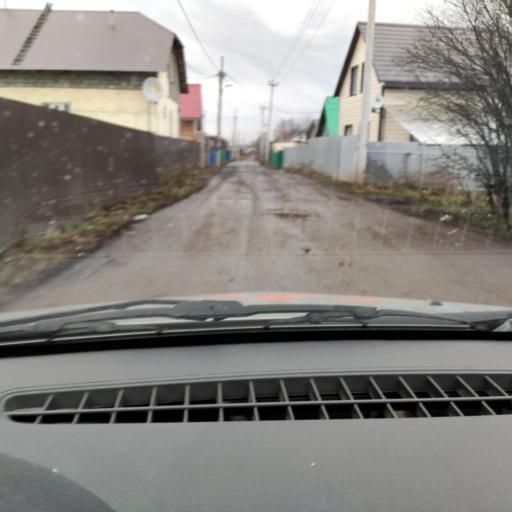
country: RU
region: Bashkortostan
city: Mikhaylovka
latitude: 54.8400
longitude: 55.9468
